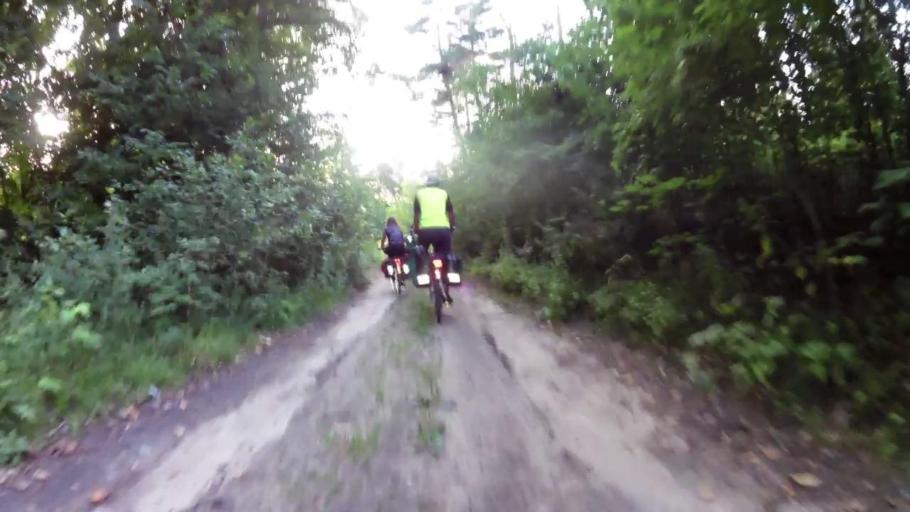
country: PL
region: West Pomeranian Voivodeship
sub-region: Powiat drawski
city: Drawsko Pomorskie
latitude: 53.4999
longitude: 15.7403
